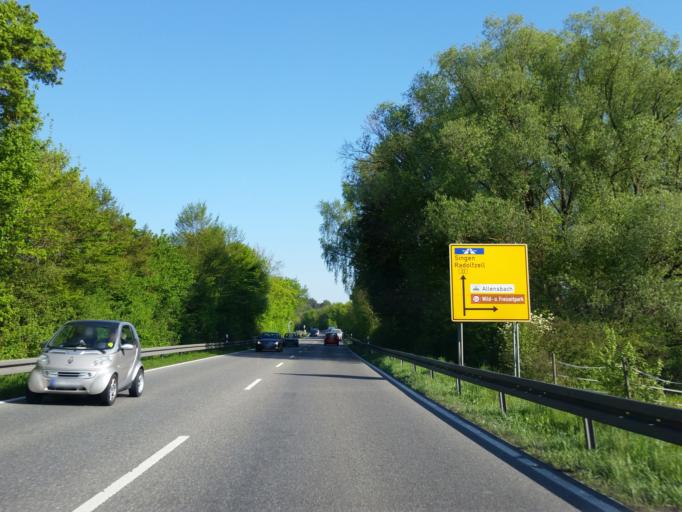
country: DE
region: Baden-Wuerttemberg
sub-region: Freiburg Region
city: Allensbach
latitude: 47.7185
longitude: 9.0743
